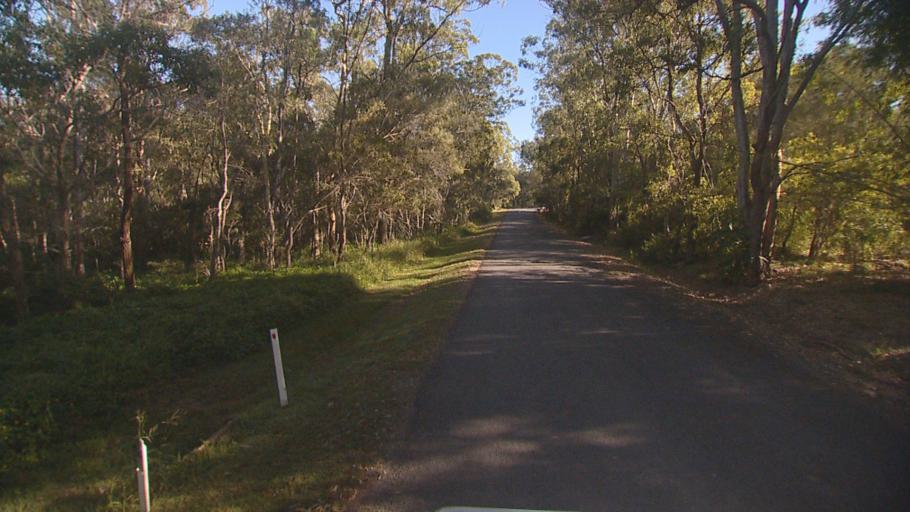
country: AU
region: Queensland
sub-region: Gold Coast
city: Yatala
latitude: -27.6893
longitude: 153.2788
